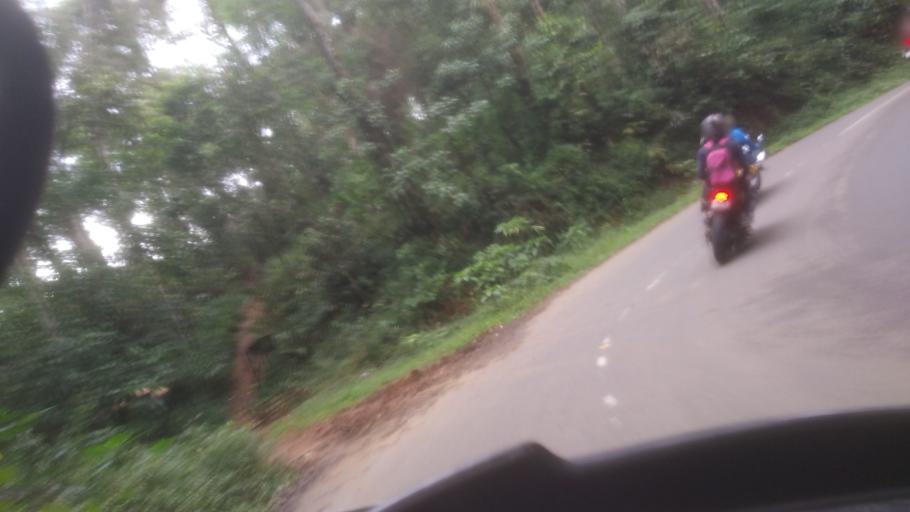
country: IN
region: Tamil Nadu
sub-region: Theni
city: Kombai
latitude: 9.8943
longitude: 77.1578
